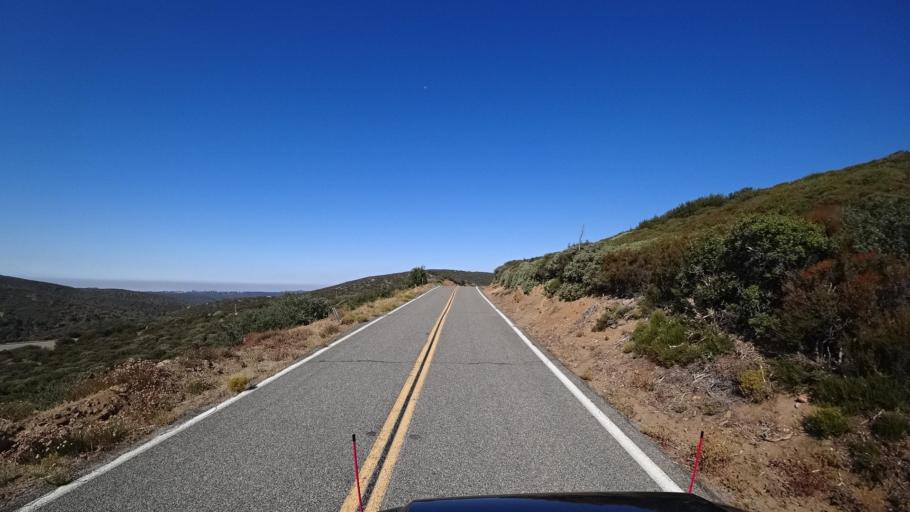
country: US
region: California
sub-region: San Diego County
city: Pine Valley
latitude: 32.9355
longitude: -116.4852
